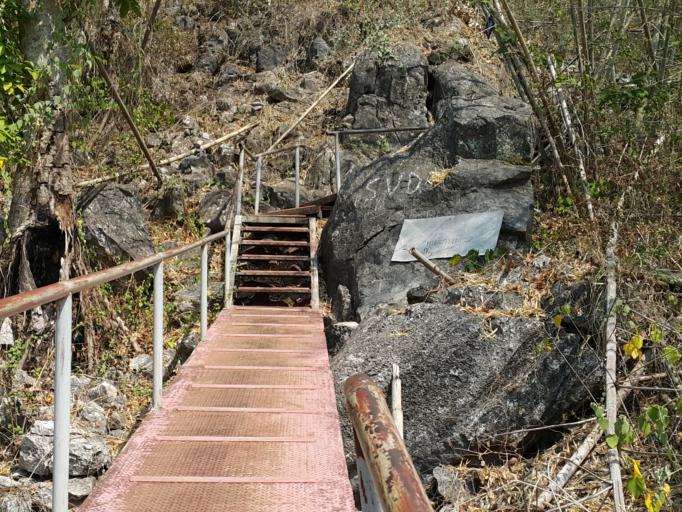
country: TH
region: Lampang
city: Mueang Pan
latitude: 18.7462
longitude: 99.5306
